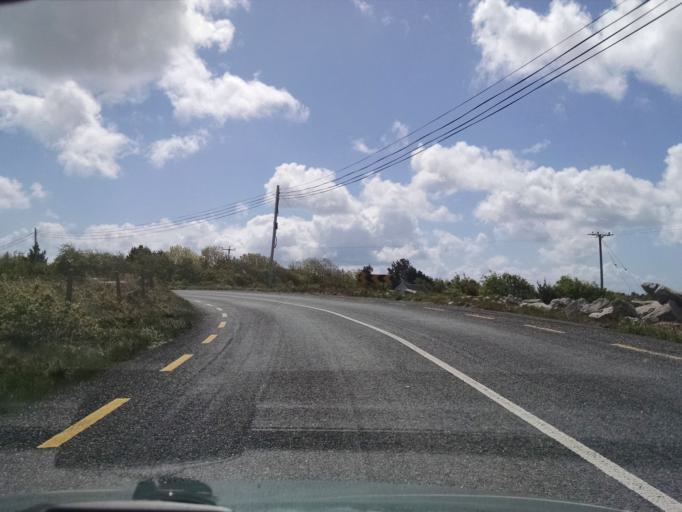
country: IE
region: Connaught
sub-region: County Galway
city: Oughterard
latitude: 53.3078
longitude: -9.5976
